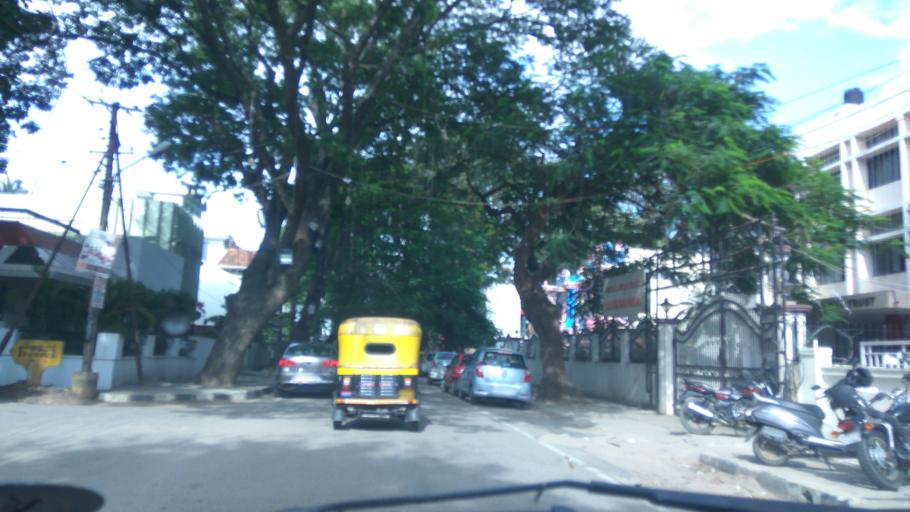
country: IN
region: Karnataka
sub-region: Bangalore Urban
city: Bangalore
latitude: 12.9686
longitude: 77.6419
